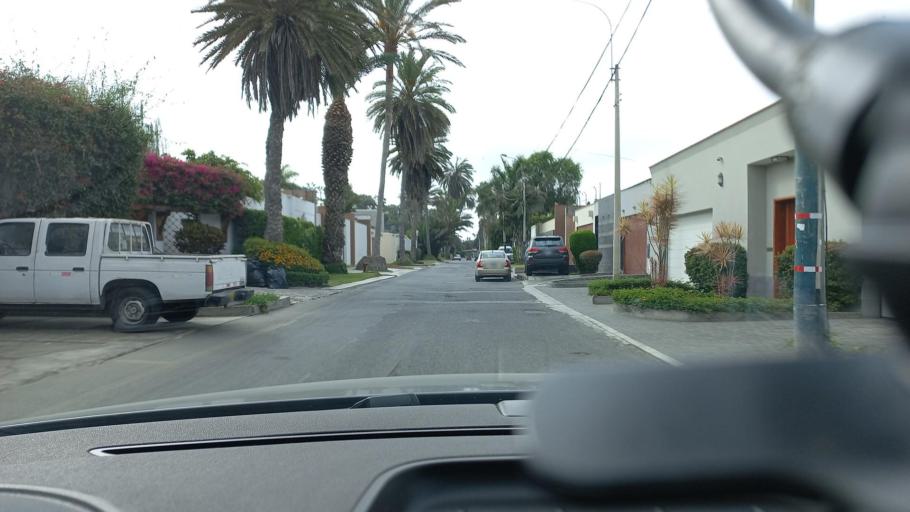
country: PE
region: Lima
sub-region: Lima
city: Surco
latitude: -12.2083
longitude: -77.0075
